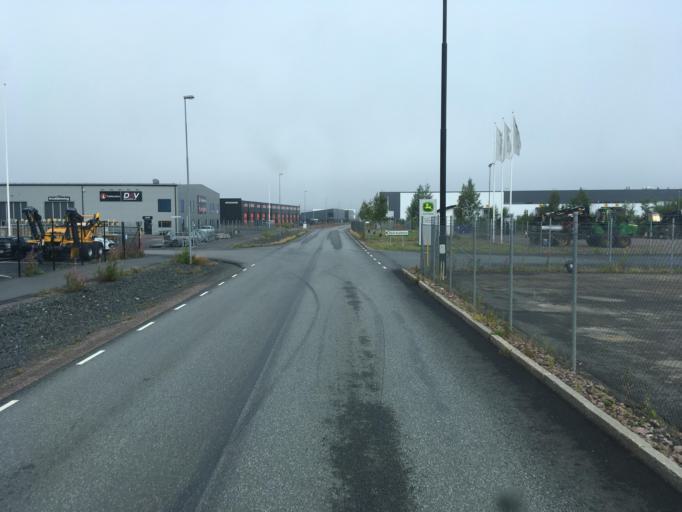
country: SE
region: Joenkoeping
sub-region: Jonkopings Kommun
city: Jonkoping
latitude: 57.7656
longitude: 14.0903
